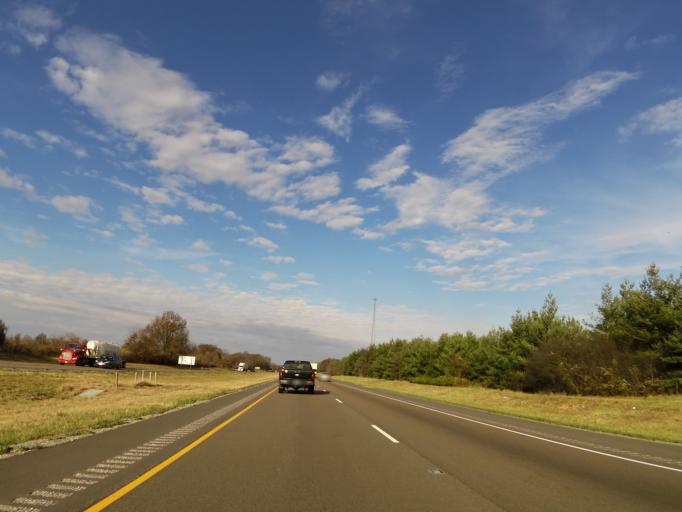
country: US
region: Illinois
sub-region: Washington County
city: Okawville
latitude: 38.4524
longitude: -89.5537
